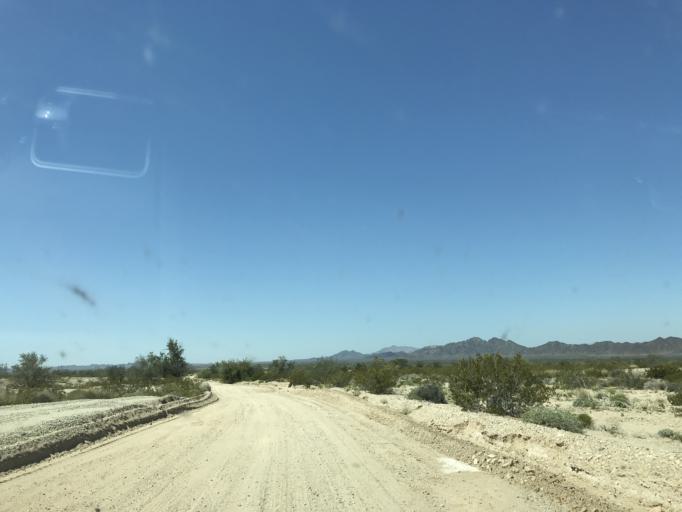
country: US
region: California
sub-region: Riverside County
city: Mesa Verde
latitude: 33.4986
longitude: -114.8679
